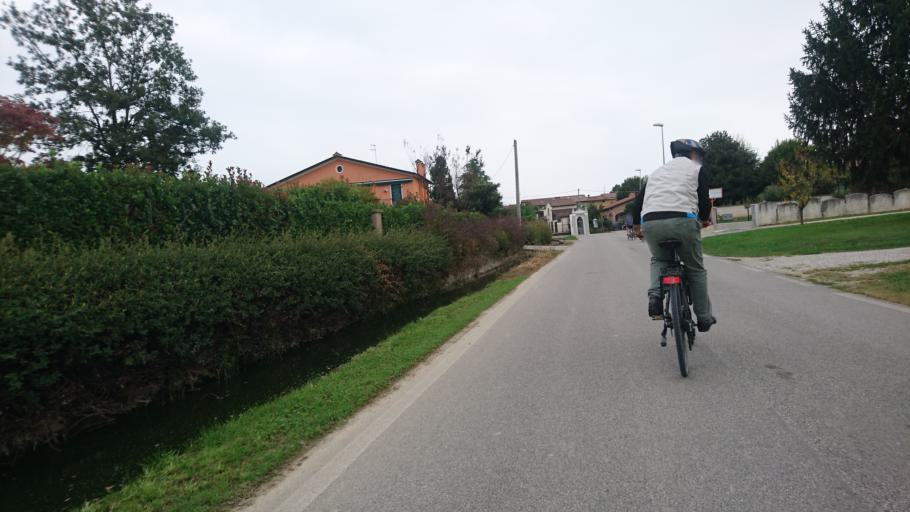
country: IT
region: Veneto
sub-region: Provincia di Padova
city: Santa Maria di Non
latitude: 45.5191
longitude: 11.8510
